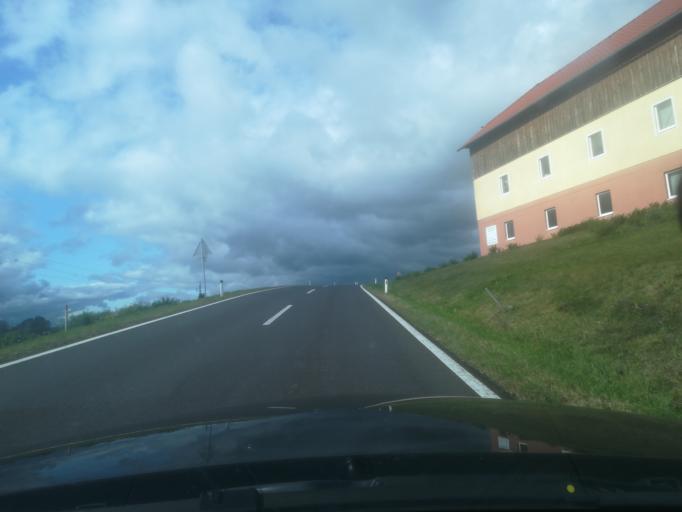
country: AT
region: Upper Austria
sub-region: Politischer Bezirk Urfahr-Umgebung
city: Gramastetten
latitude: 48.3952
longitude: 14.1821
